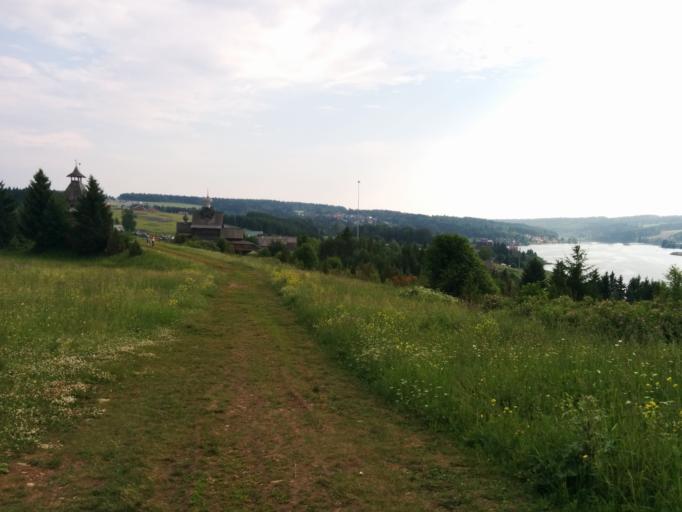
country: RU
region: Perm
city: Polazna
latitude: 58.2621
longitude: 56.2606
